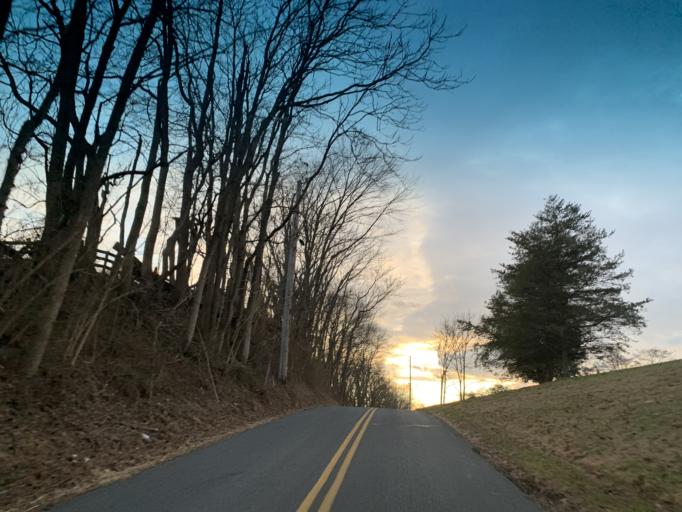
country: US
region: Maryland
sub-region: Harford County
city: Bel Air North
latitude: 39.6198
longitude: -76.3104
